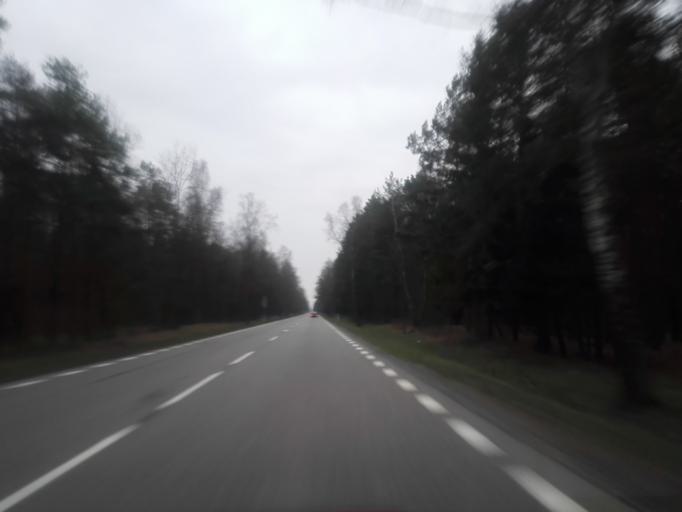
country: PL
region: Podlasie
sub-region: Powiat kolnenski
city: Stawiski
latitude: 53.3482
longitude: 22.1592
